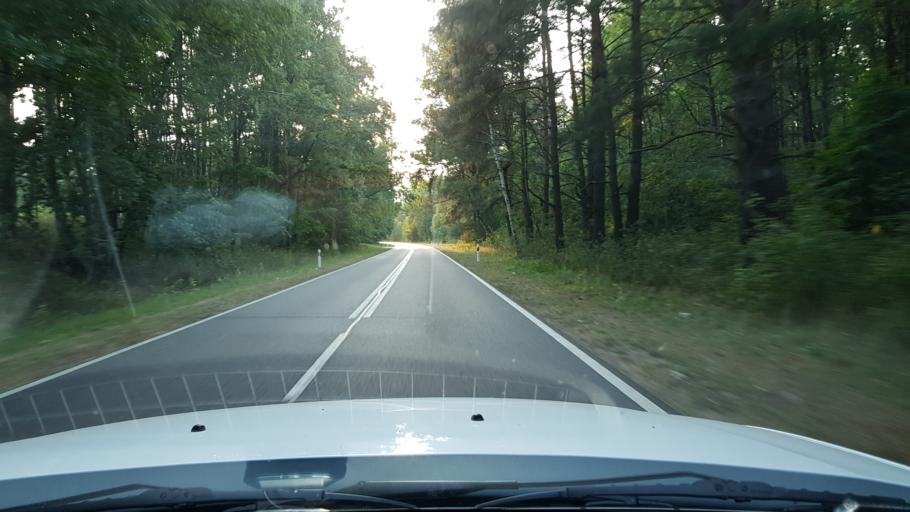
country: PL
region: West Pomeranian Voivodeship
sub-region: Powiat stargardzki
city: Stara Dabrowa
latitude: 53.4332
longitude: 15.2083
